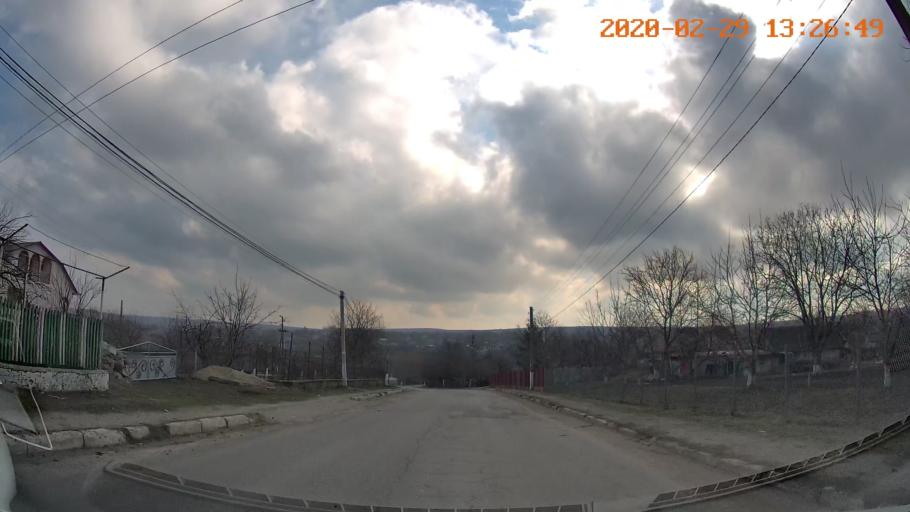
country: MD
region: Telenesti
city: Camenca
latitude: 47.9168
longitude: 28.6392
